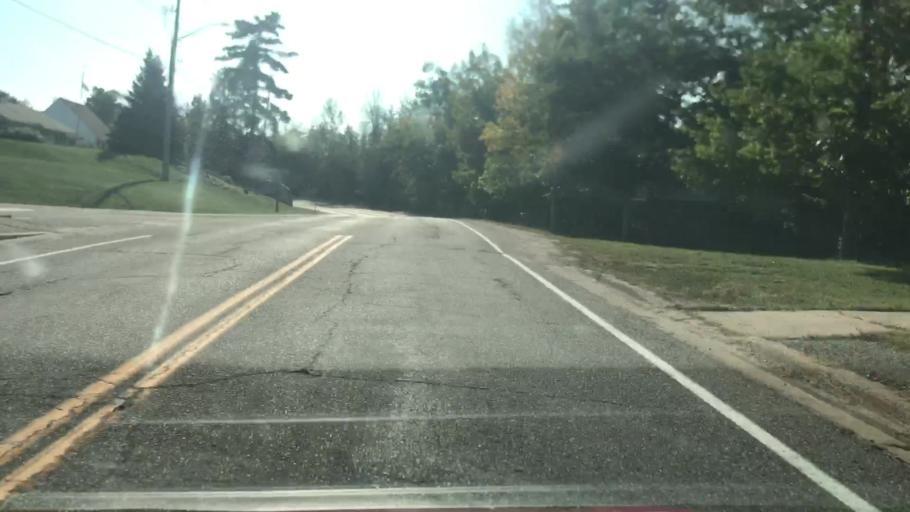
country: US
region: Michigan
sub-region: Chippewa County
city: Sault Ste. Marie
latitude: 46.2916
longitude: -84.0388
